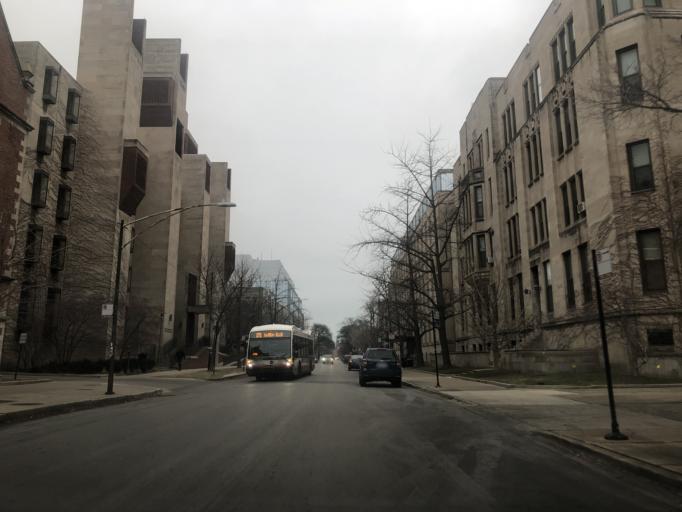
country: US
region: Illinois
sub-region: Cook County
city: Chicago
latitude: 41.7896
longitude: -87.6013
